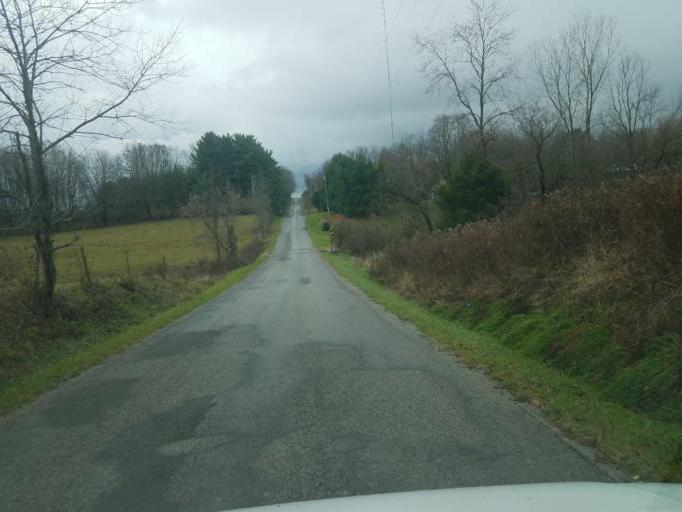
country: US
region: Ohio
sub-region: Morrow County
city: Mount Gilead
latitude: 40.5900
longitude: -82.8050
